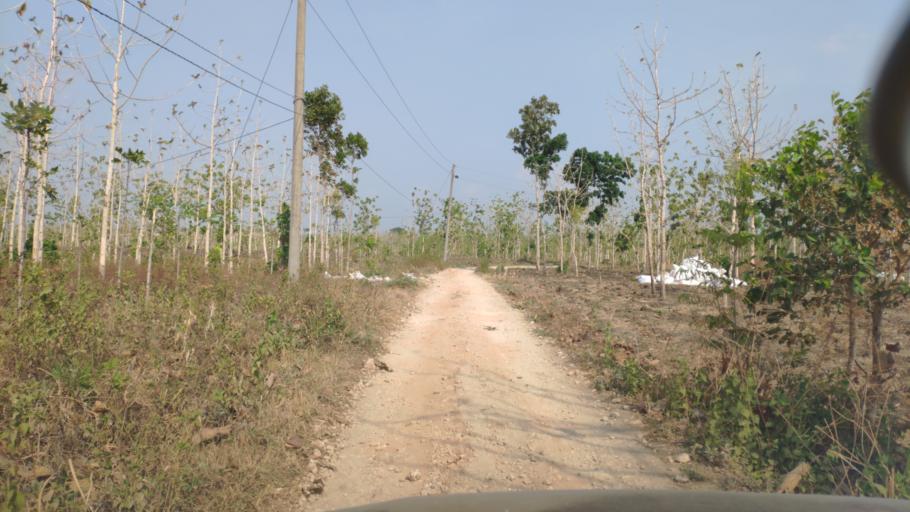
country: ID
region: Central Java
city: Jomblang
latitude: -7.0247
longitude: 111.4518
